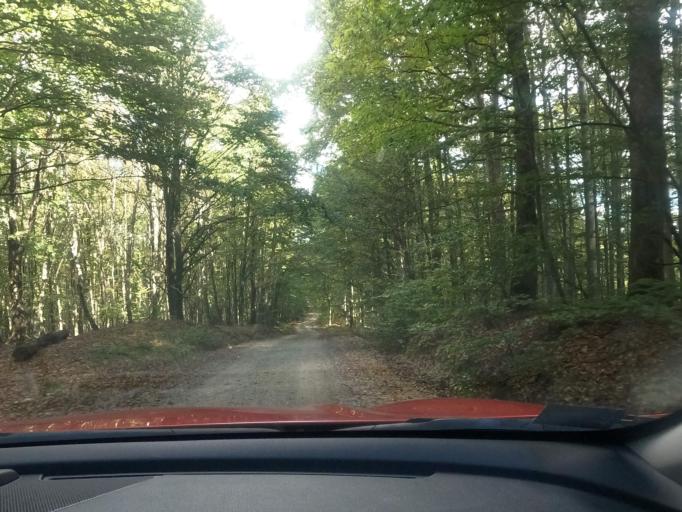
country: BA
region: Federation of Bosnia and Herzegovina
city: Velika Kladusa
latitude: 45.2545
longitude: 15.7723
